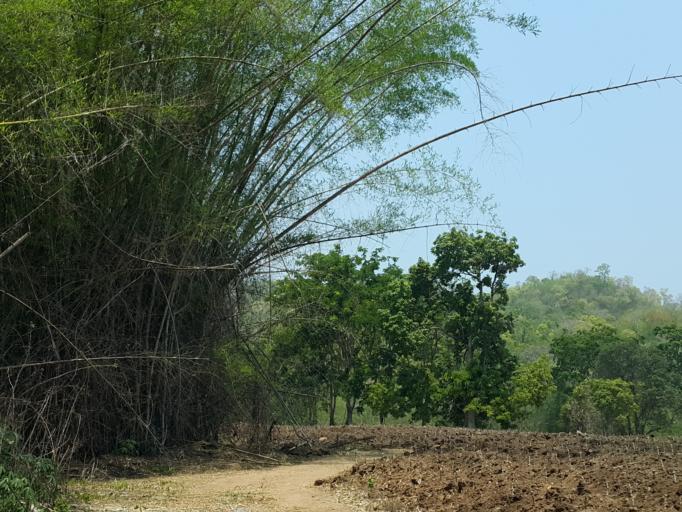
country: TH
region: Kanchanaburi
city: Sai Yok
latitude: 14.2150
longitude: 98.8750
